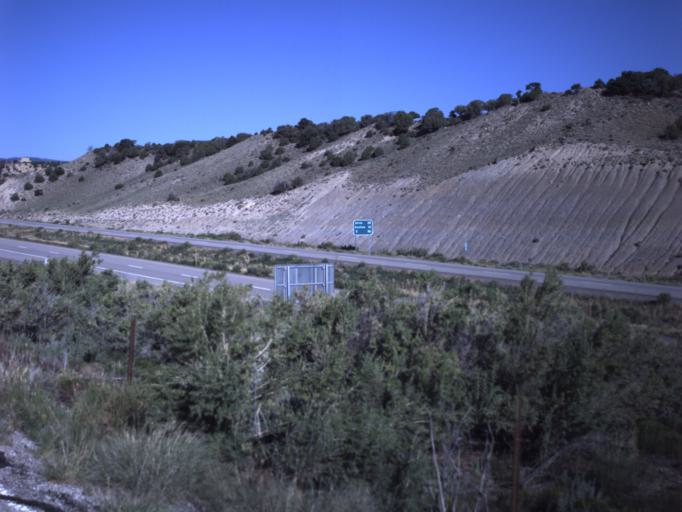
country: US
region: Utah
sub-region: Emery County
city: Ferron
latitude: 38.7609
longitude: -111.3663
